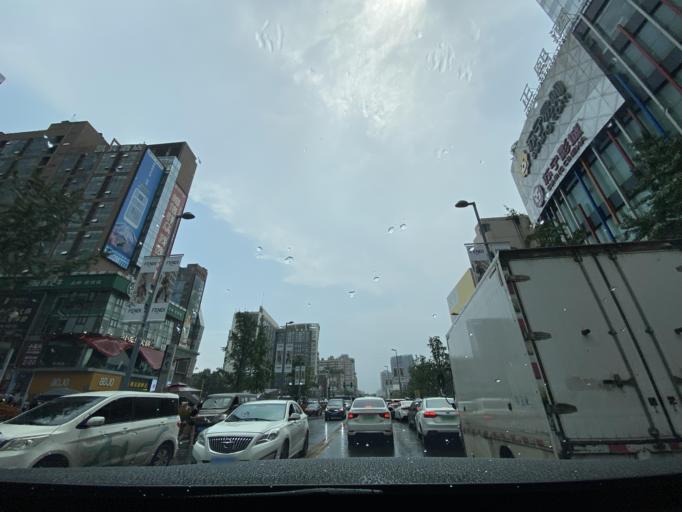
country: CN
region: Sichuan
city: Chengdu
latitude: 30.6559
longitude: 104.0765
